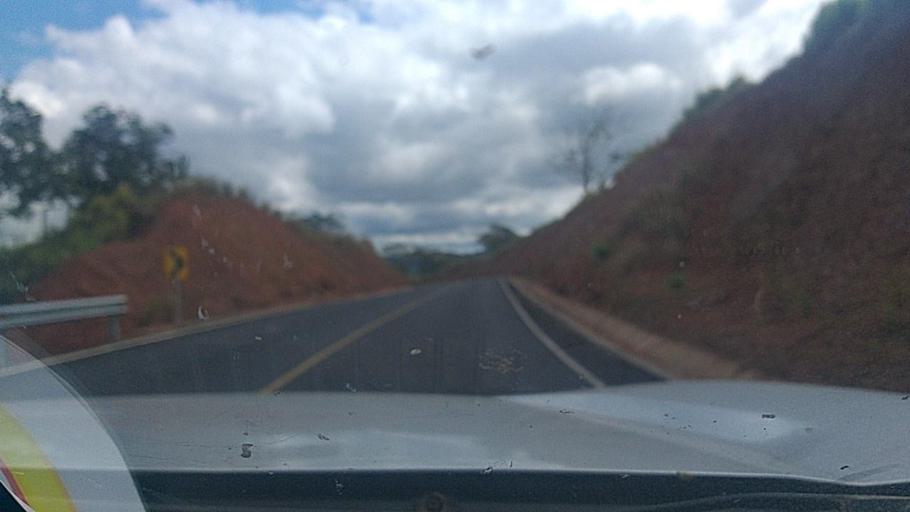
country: NI
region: Atlantico Sur
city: Muelle de los Bueyes
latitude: 12.1293
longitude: -84.4350
